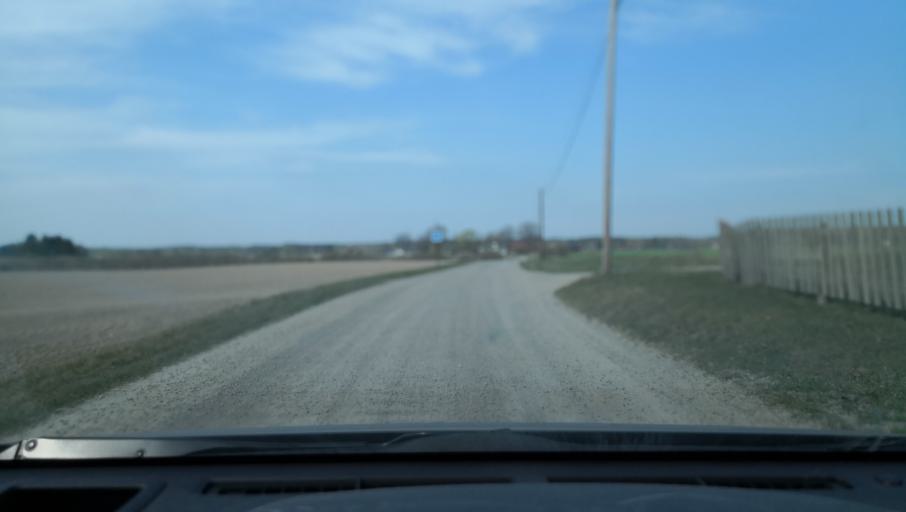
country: SE
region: Vaestmanland
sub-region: Vasteras
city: Skultuna
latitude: 59.7921
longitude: 16.4424
